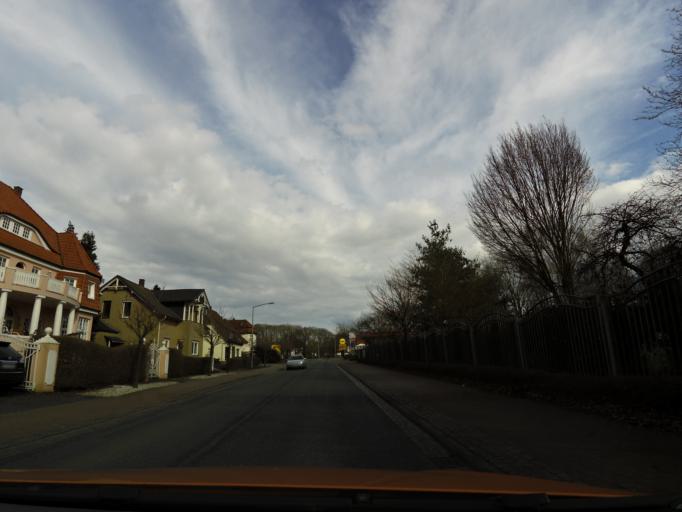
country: DE
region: Lower Saxony
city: Harpstedt
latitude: 52.9103
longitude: 8.5967
